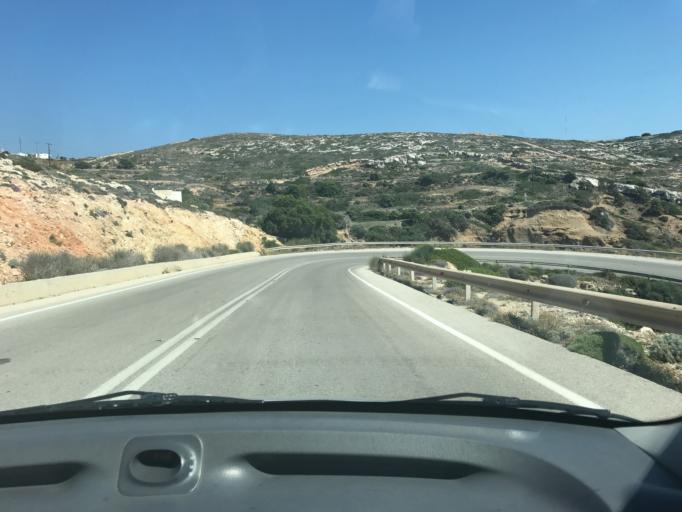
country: GR
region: South Aegean
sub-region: Nomos Dodekanisou
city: Karpathos
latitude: 35.4714
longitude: 27.1194
